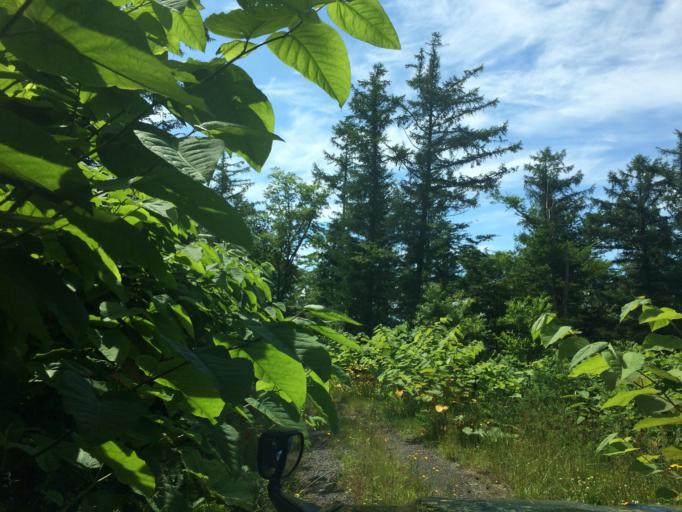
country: JP
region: Hokkaido
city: Niseko Town
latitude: 42.8655
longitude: 140.7955
